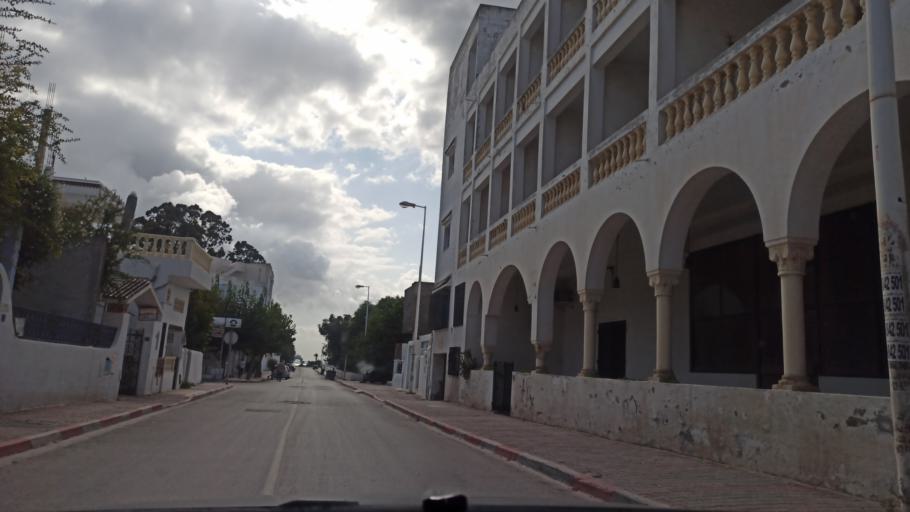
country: TN
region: Nabul
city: Al Hammamat
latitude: 36.3954
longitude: 10.6149
